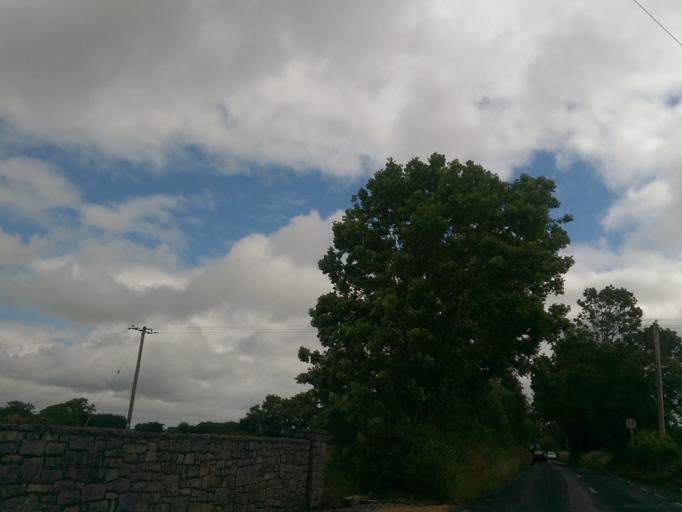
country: IE
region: Connaught
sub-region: County Galway
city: Loughrea
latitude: 53.4193
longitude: -8.5100
